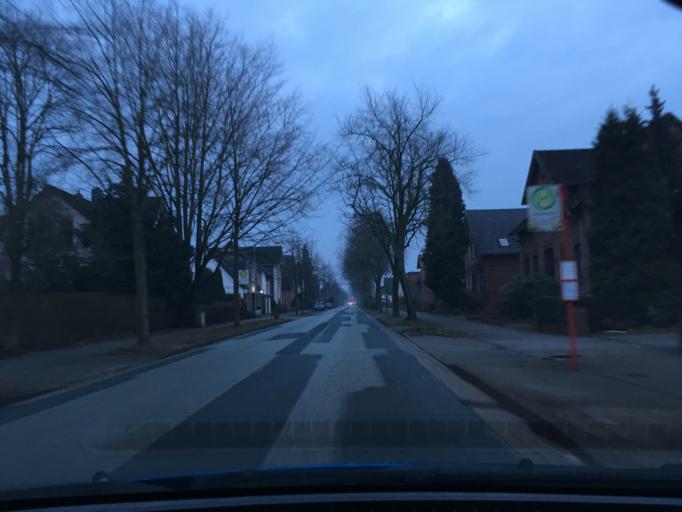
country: DE
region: Lower Saxony
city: Winsen
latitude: 53.3719
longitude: 10.1963
